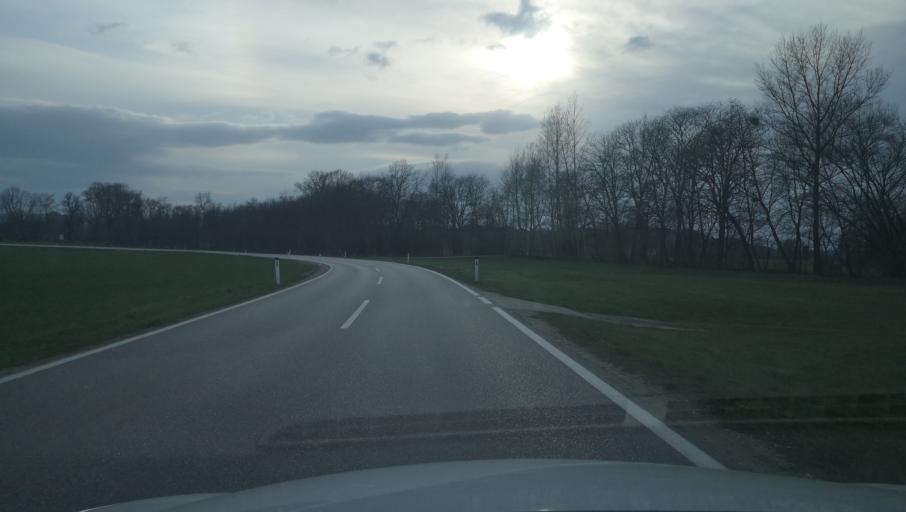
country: AT
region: Lower Austria
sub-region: Politischer Bezirk Amstetten
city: Euratsfeld
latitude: 48.0997
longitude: 14.9316
